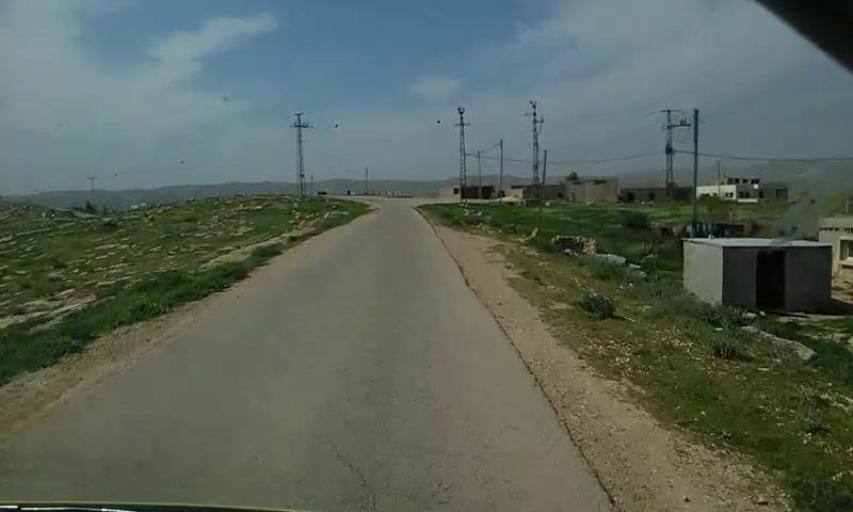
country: PS
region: West Bank
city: Khallat al Mayyah
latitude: 31.4416
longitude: 35.1984
